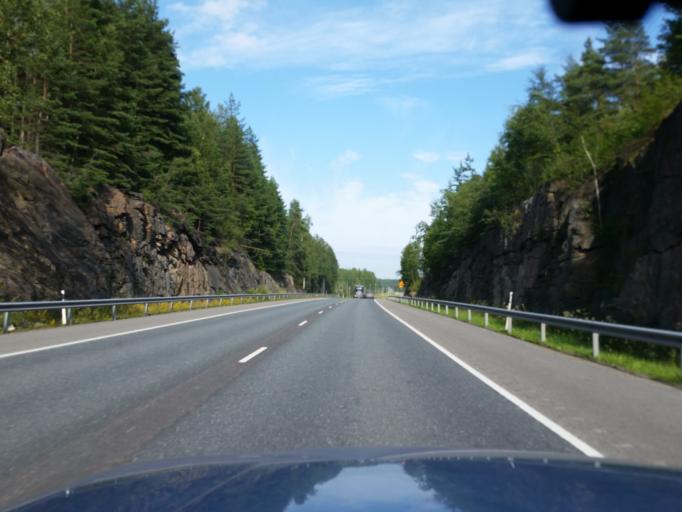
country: FI
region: Uusimaa
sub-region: Helsinki
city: Siuntio
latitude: 60.0914
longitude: 24.2192
